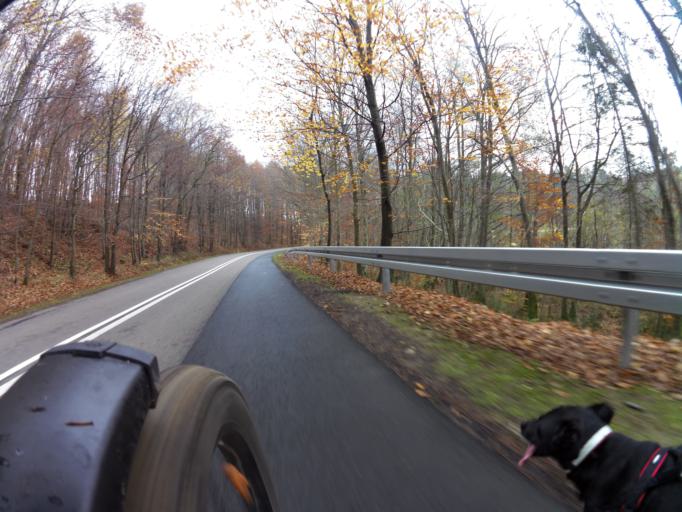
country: PL
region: Pomeranian Voivodeship
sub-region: Powiat wejherowski
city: Orle
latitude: 54.6886
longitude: 18.1470
